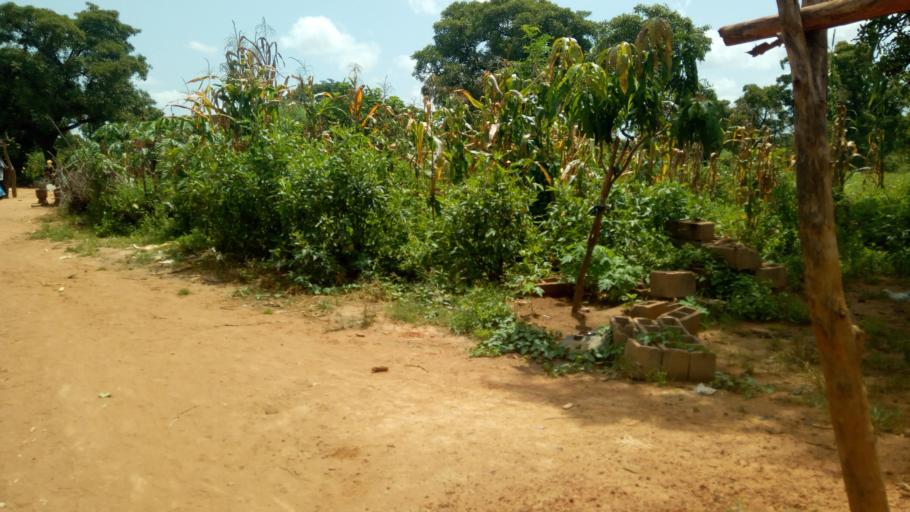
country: ML
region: Sikasso
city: Yorosso
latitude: 12.2013
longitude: -4.9151
